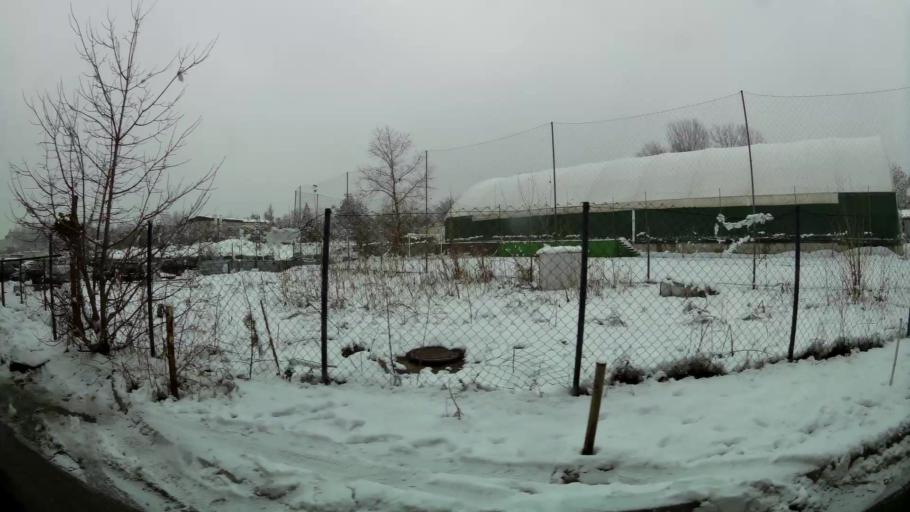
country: RS
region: Central Serbia
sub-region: Belgrade
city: Novi Beograd
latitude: 44.8233
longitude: 20.4211
